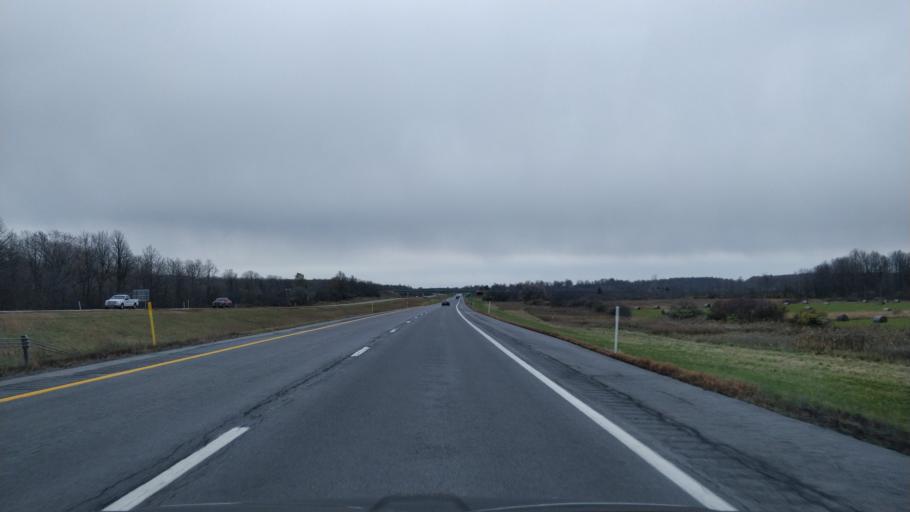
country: US
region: New York
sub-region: Jefferson County
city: Calcium
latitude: 44.0804
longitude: -75.9162
